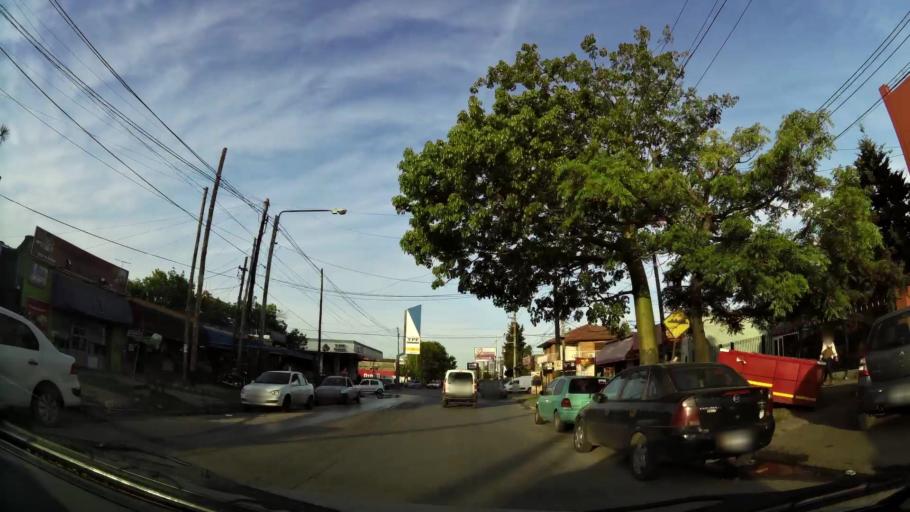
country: AR
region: Buenos Aires
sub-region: Partido de Almirante Brown
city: Adrogue
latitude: -34.7924
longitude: -58.3582
